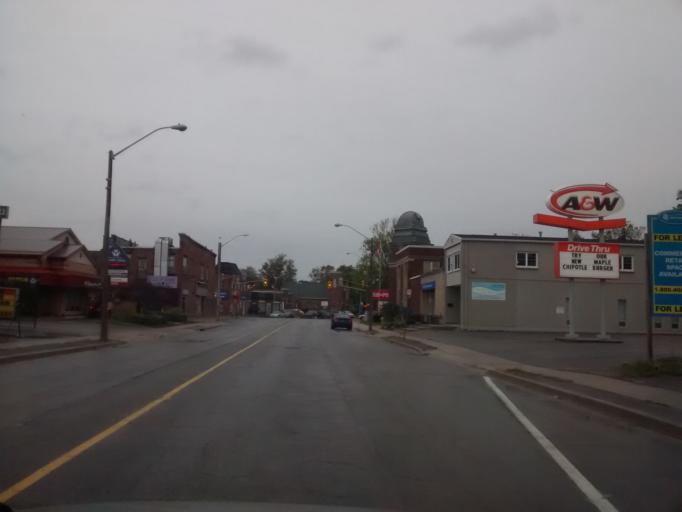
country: CA
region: Ontario
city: Welland
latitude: 42.9035
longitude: -79.6157
